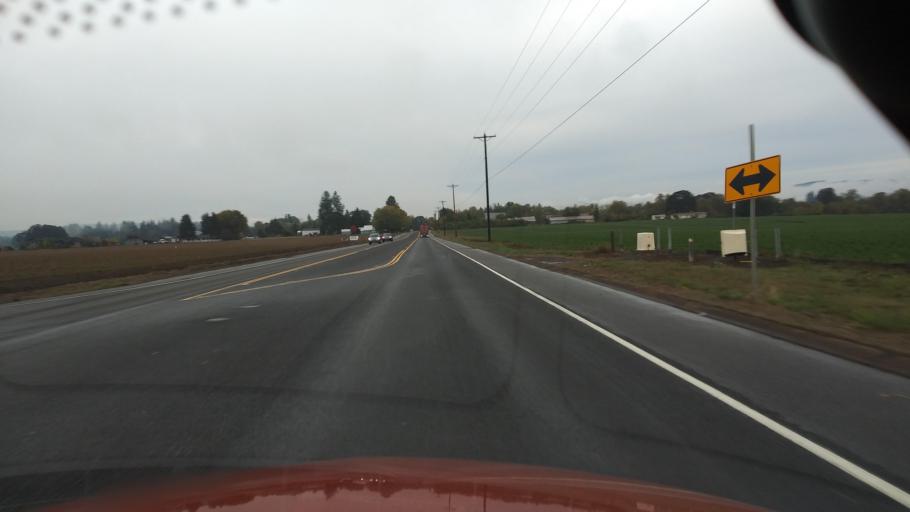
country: US
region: Oregon
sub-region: Washington County
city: Cornelius
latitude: 45.5621
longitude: -123.0552
